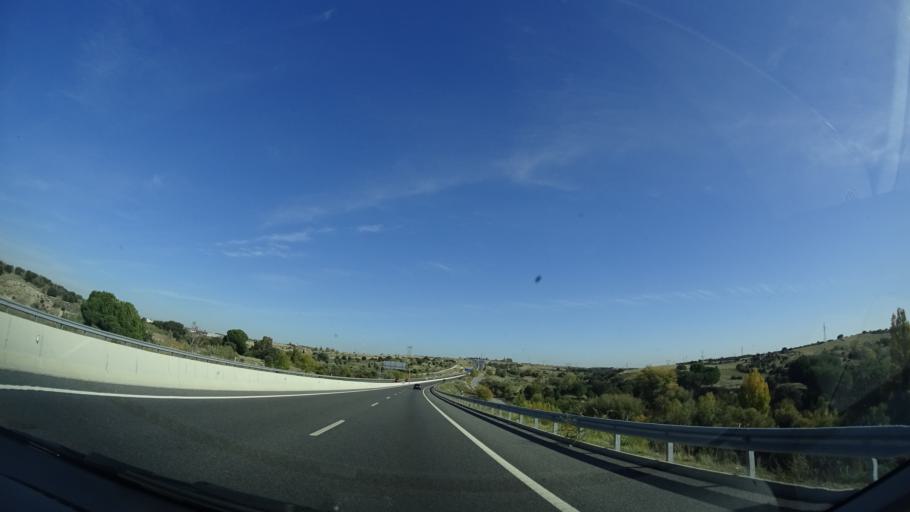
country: ES
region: Madrid
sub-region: Provincia de Madrid
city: Las Rozas de Madrid
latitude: 40.4805
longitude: -3.9142
